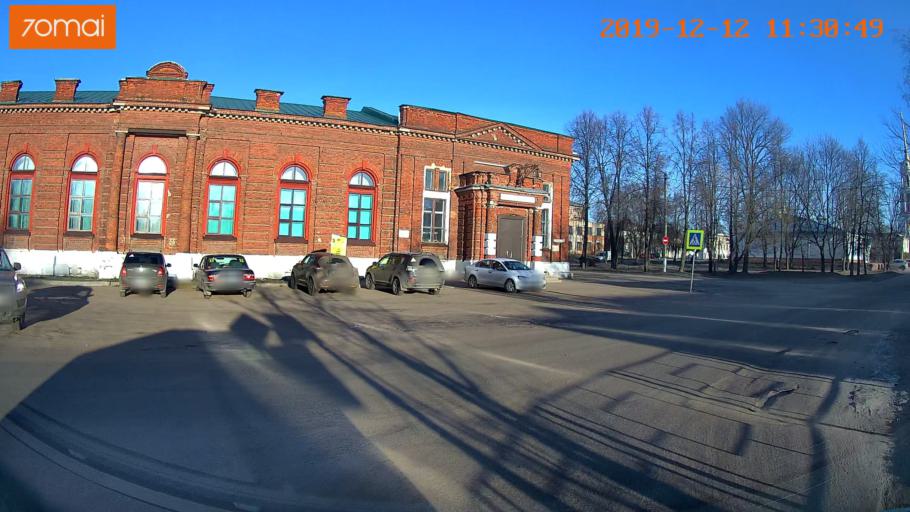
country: RU
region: Ivanovo
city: Shuya
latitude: 56.8555
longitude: 41.3784
